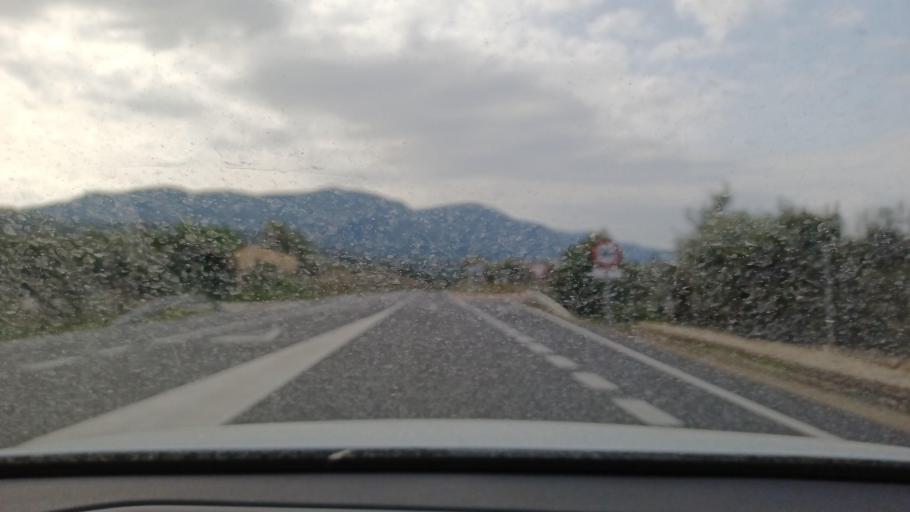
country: ES
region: Catalonia
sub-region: Provincia de Tarragona
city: Masdenverge
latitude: 40.6773
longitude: 0.5259
